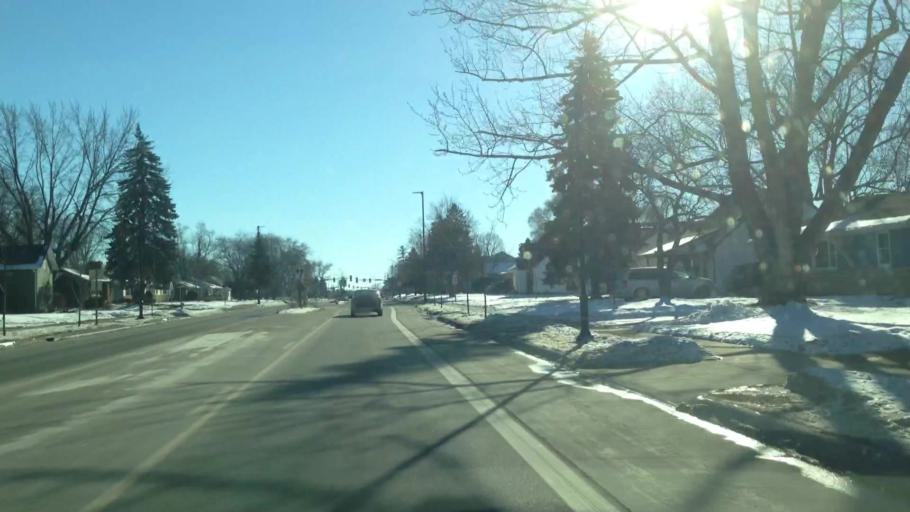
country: US
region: Minnesota
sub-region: Hennepin County
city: Richfield
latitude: 44.8682
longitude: -93.2681
